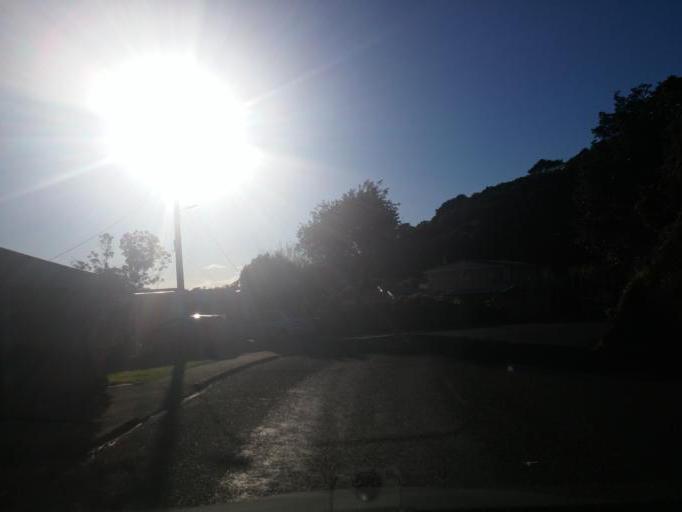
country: NZ
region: Wellington
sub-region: Wellington City
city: Kelburn
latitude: -41.2708
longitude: 174.7615
